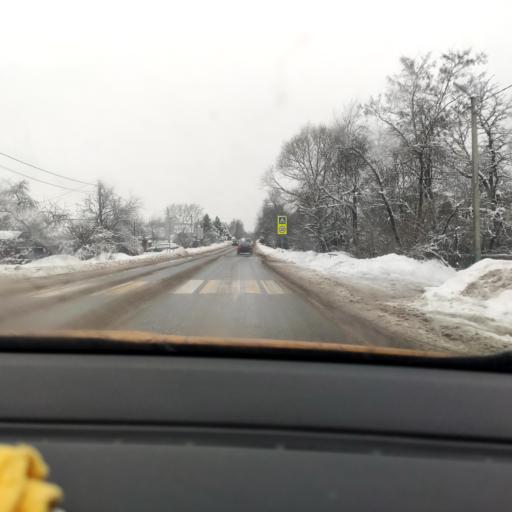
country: RU
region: Moskovskaya
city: Zvenigorod
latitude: 55.7489
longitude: 36.8770
